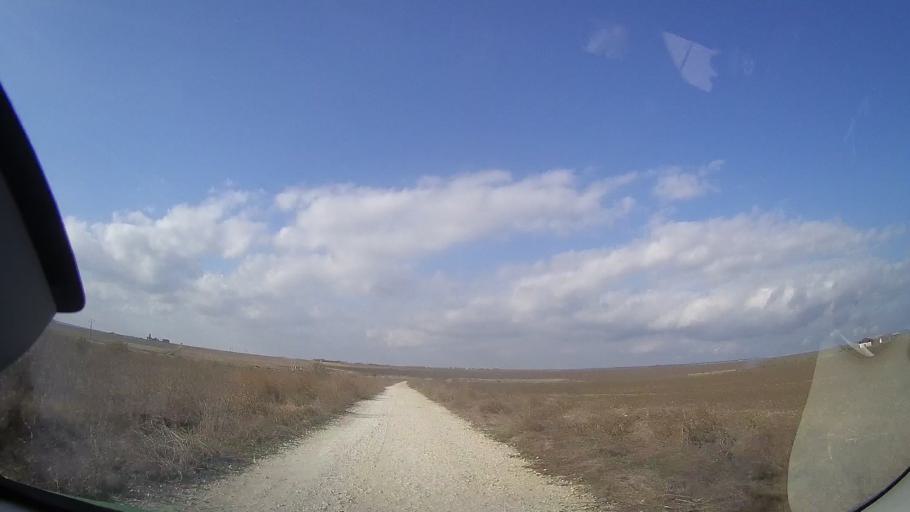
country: RO
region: Constanta
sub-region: Comuna Douazeci si Trei August
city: Douazeci si Trei August
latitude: 43.9068
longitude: 28.6126
